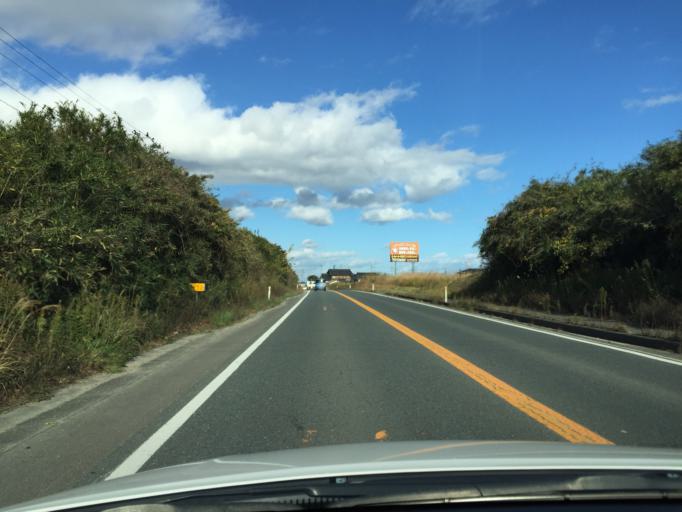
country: JP
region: Fukushima
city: Namie
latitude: 37.5818
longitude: 141.0095
